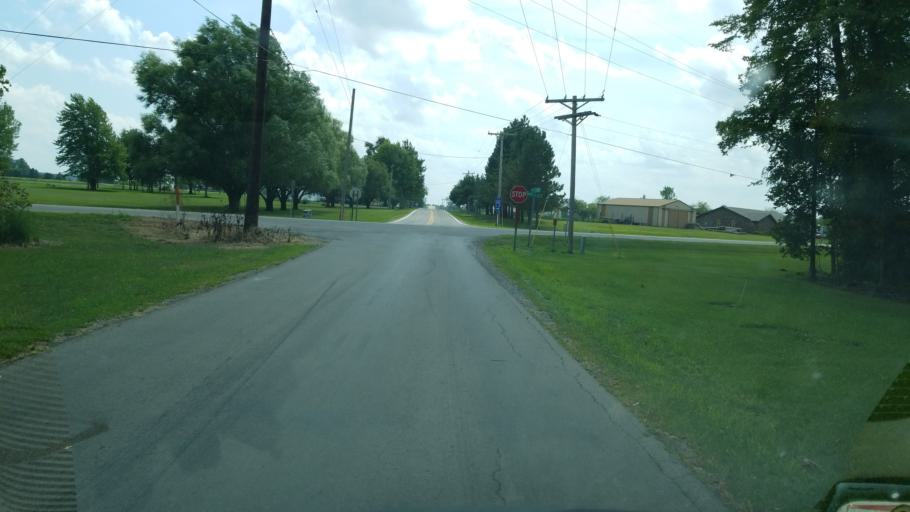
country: US
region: Ohio
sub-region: Hancock County
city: Findlay
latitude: 40.9857
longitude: -83.7275
